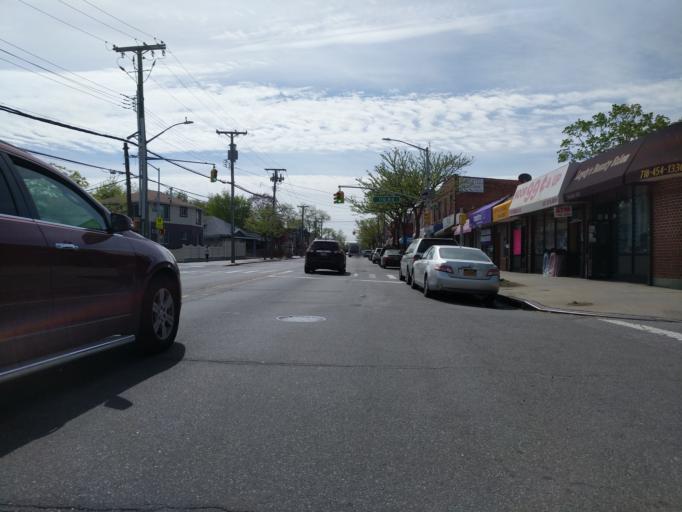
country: US
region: New York
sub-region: Queens County
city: Jamaica
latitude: 40.7025
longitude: -73.7664
